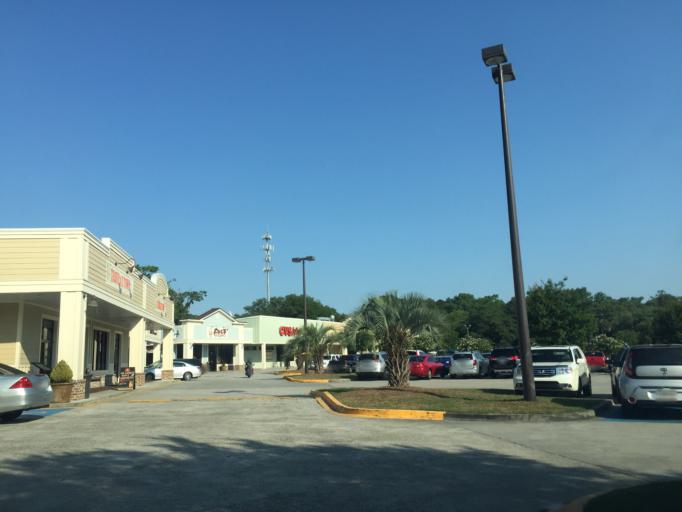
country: US
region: Georgia
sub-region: Chatham County
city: Isle of Hope
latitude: 31.9878
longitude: -81.0745
